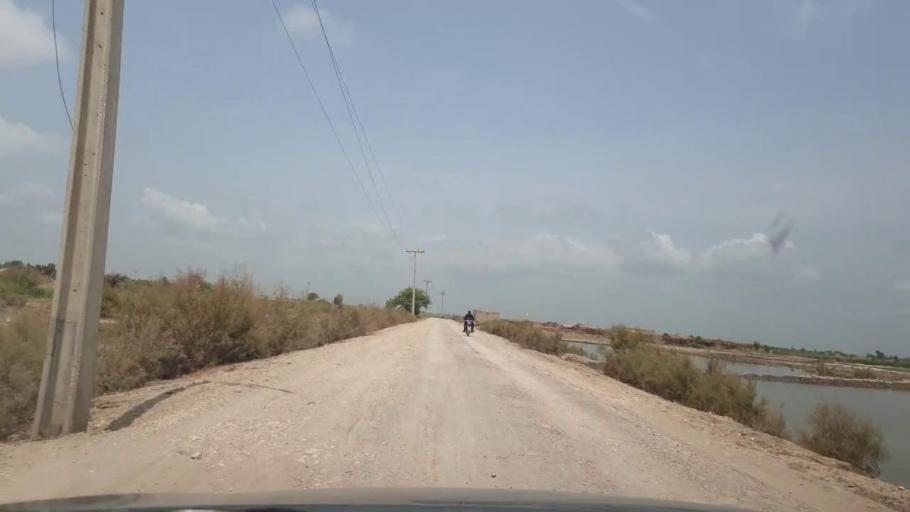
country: PK
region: Sindh
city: Ratodero
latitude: 27.9077
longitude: 68.3104
